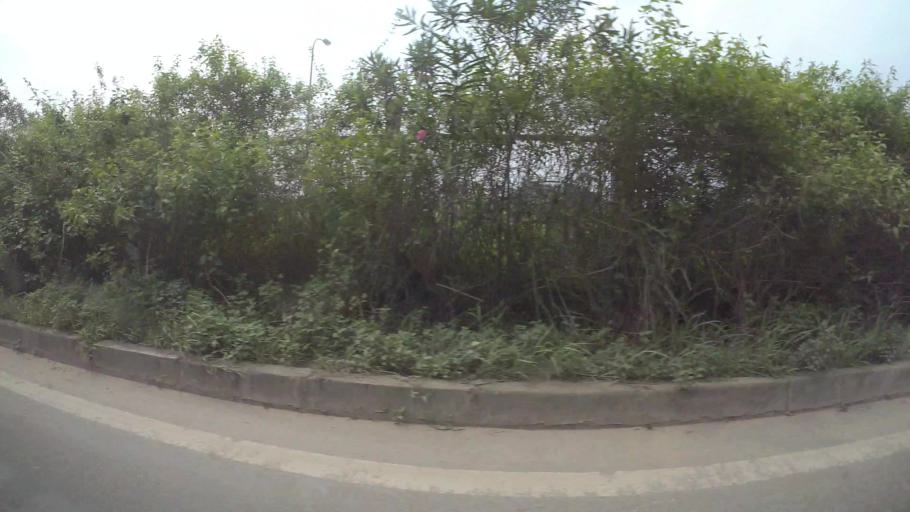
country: VN
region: Ha Noi
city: Quoc Oai
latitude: 21.0034
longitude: 105.6540
